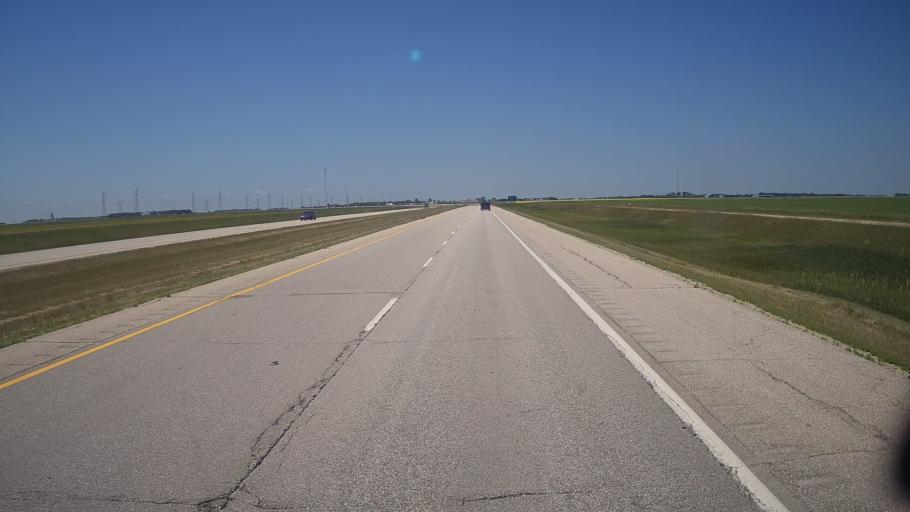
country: CA
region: Manitoba
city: Stonewall
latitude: 49.9900
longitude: -97.2887
